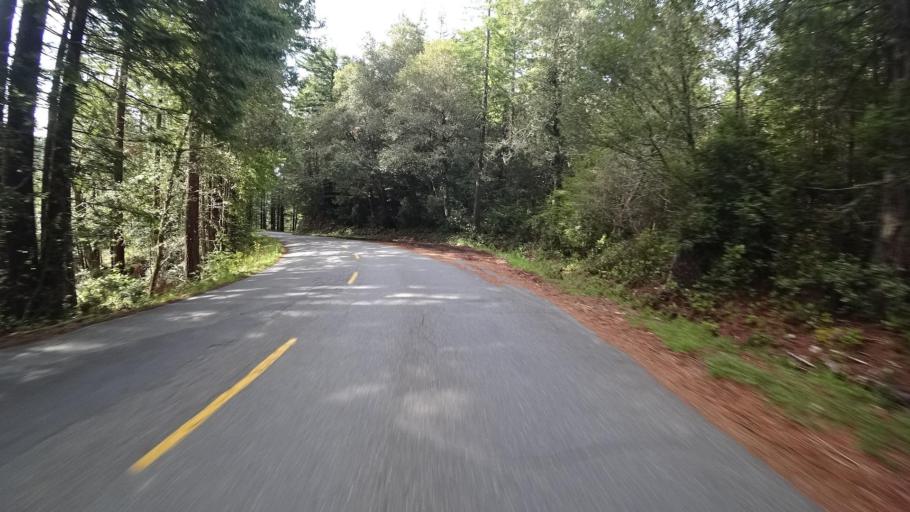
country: US
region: California
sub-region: Humboldt County
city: Bayside
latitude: 40.7581
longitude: -124.0190
